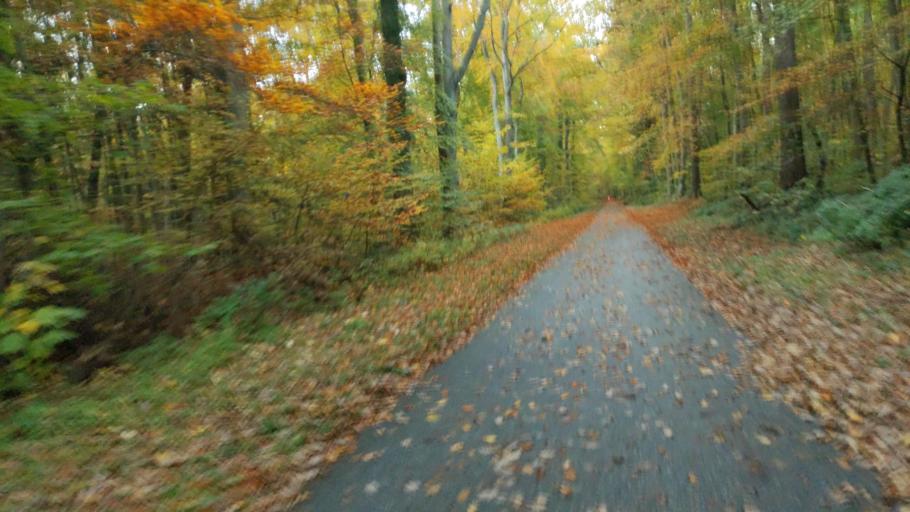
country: DE
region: Schleswig-Holstein
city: Luebeck
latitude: 53.8793
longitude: 10.7518
